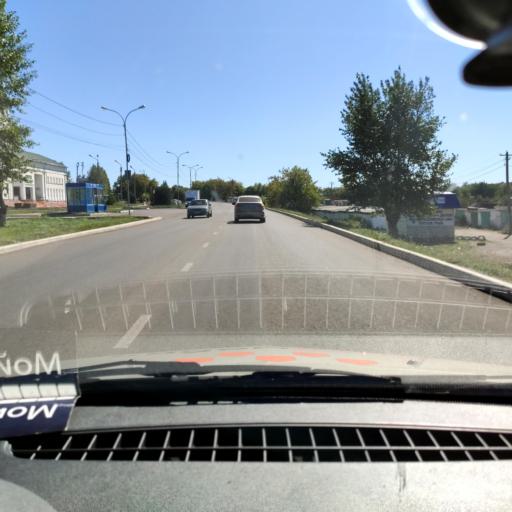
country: RU
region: Bashkortostan
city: Kumertau
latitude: 52.7599
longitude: 55.8095
